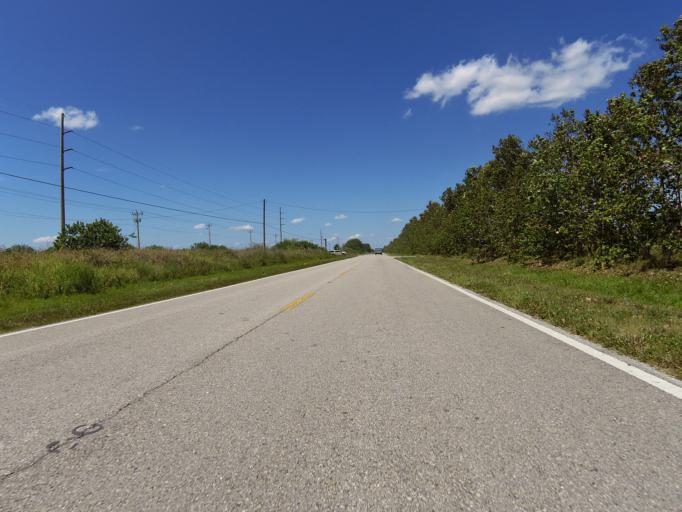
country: US
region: Florida
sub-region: Collier County
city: Immokalee
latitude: 26.3230
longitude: -81.4165
